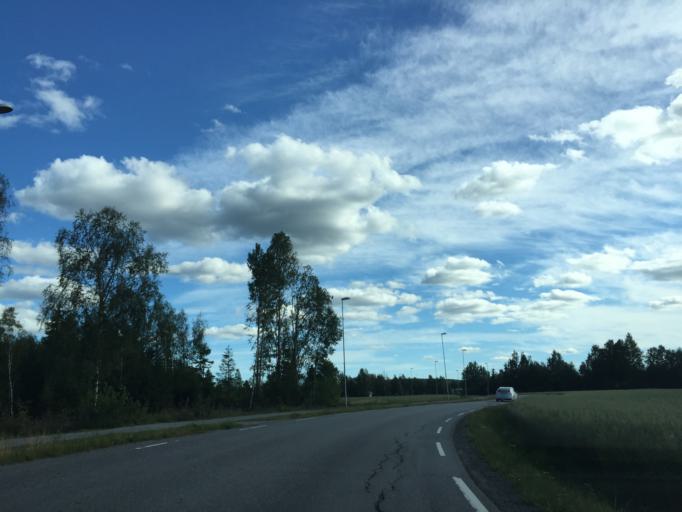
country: NO
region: Akershus
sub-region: Nes
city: Fjellfoten
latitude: 60.1023
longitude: 11.4827
